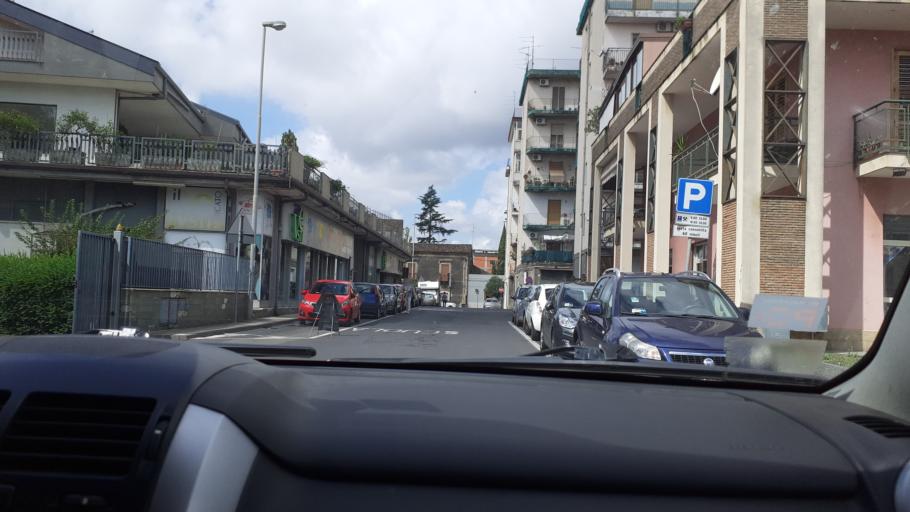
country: IT
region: Sicily
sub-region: Catania
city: San Giovanni la Punta
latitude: 37.5809
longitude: 15.0971
